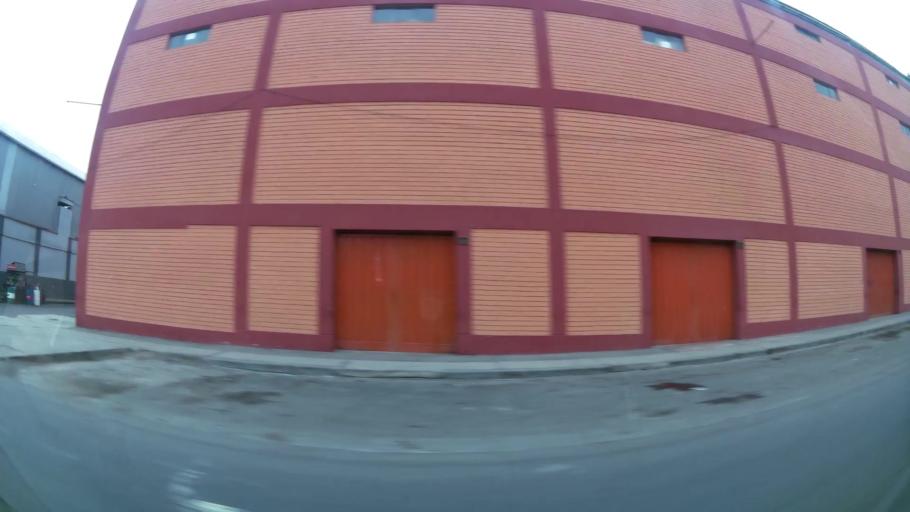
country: PE
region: Lima
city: Lima
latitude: -12.0492
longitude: -77.0525
